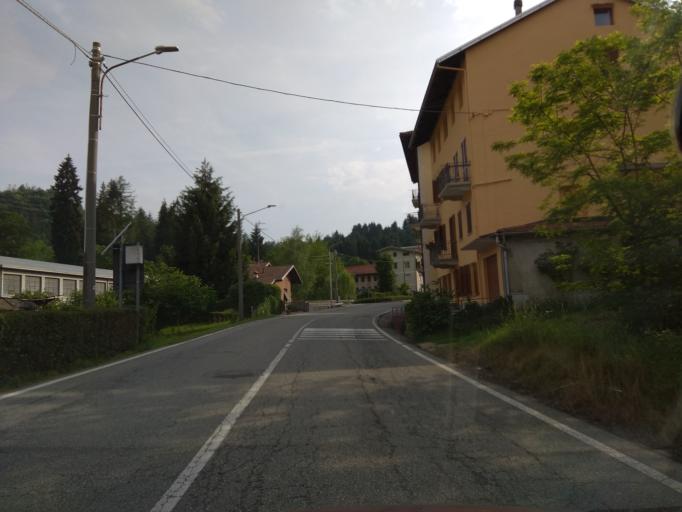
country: IT
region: Piedmont
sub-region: Provincia di Biella
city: Lanvario
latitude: 45.6561
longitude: 8.1971
